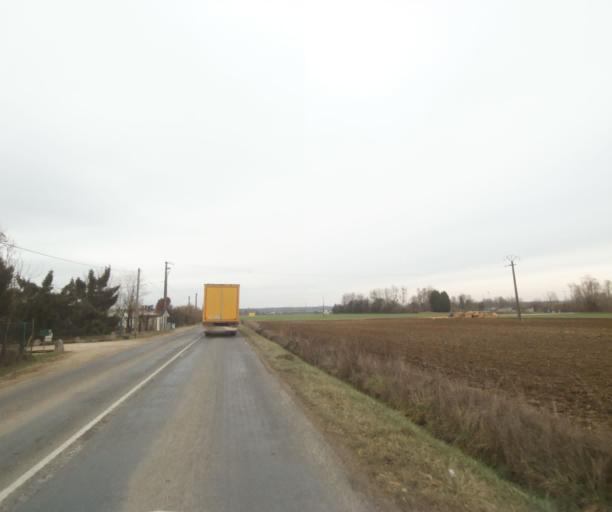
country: FR
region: Champagne-Ardenne
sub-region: Departement de la Haute-Marne
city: Villiers-en-Lieu
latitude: 48.6507
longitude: 4.9066
